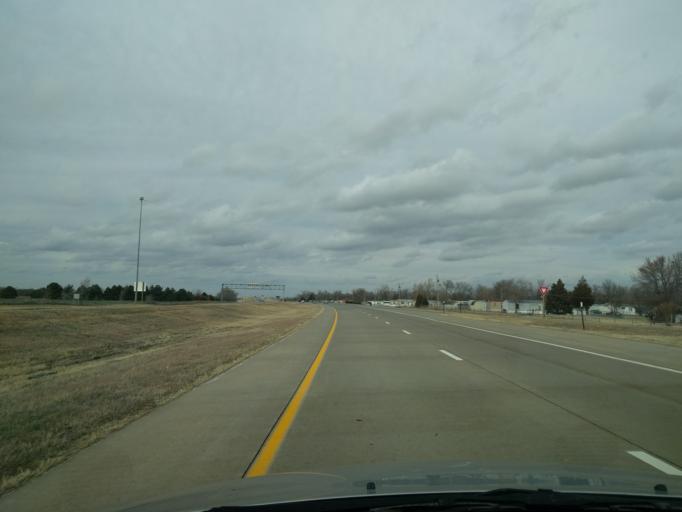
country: US
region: Kansas
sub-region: Saline County
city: Salina
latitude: 38.8003
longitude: -97.6197
